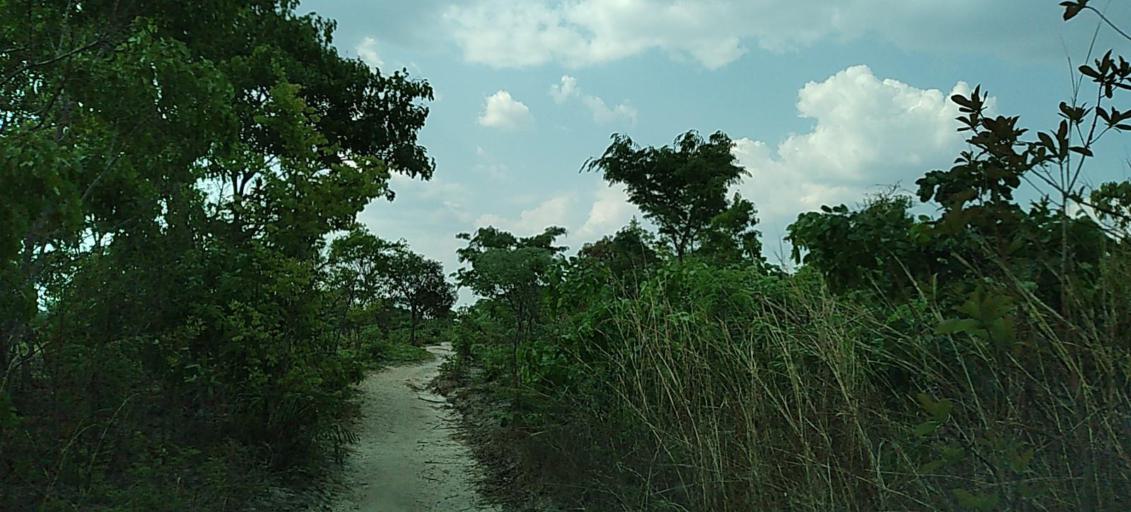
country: ZM
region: Copperbelt
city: Luanshya
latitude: -13.2202
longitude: 28.3315
